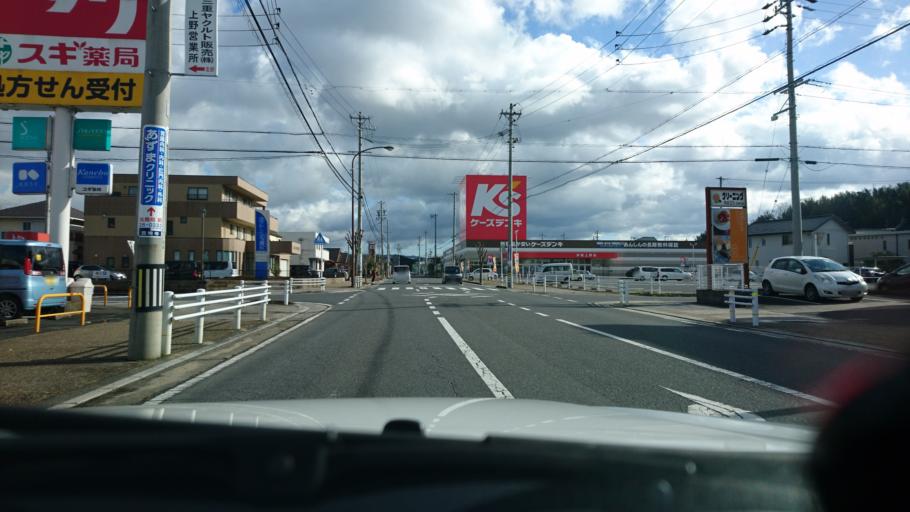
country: JP
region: Mie
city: Ueno-ebisumachi
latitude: 34.7743
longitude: 136.1310
